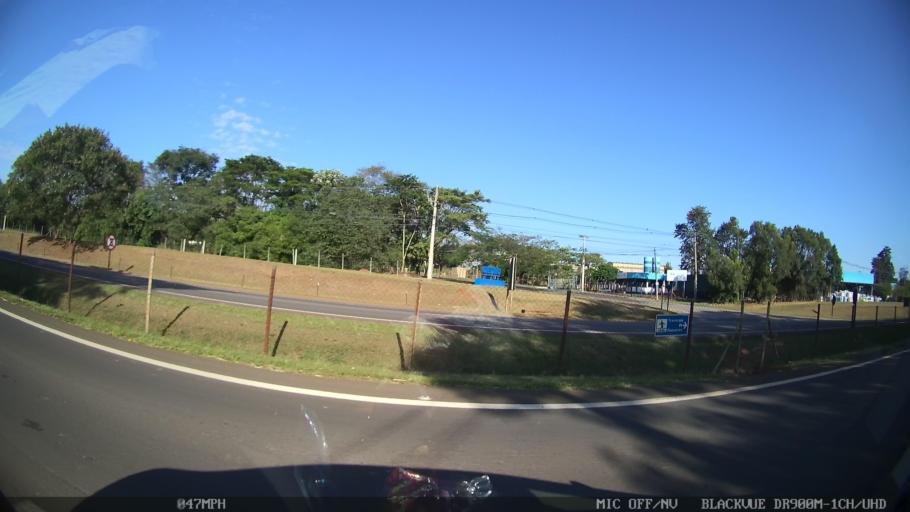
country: BR
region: Sao Paulo
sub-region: Piracicaba
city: Piracicaba
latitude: -22.6682
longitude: -47.6236
